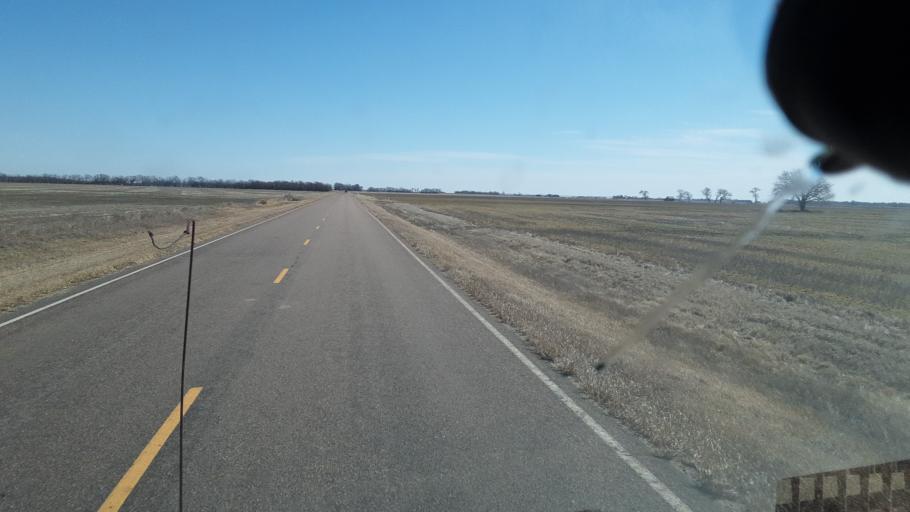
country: US
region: Kansas
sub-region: Rice County
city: Sterling
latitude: 38.2461
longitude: -98.2457
